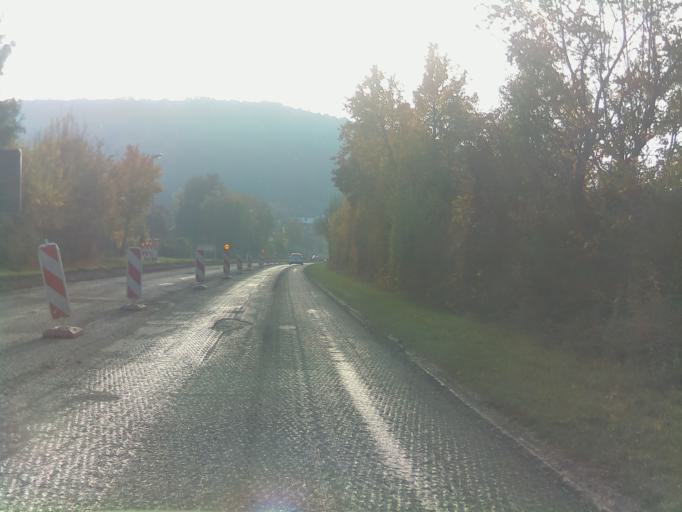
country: DE
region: Baden-Wuerttemberg
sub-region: Karlsruhe Region
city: Mosbach
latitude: 49.3827
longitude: 9.1886
